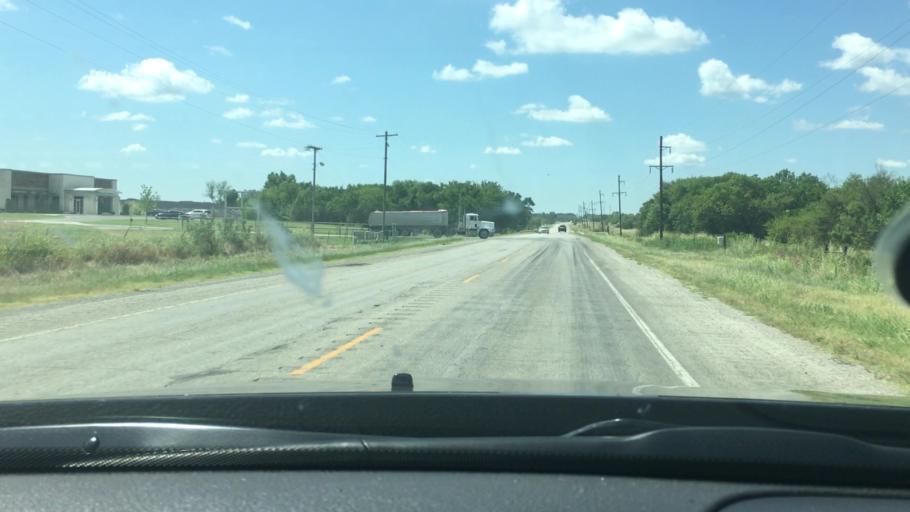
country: US
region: Oklahoma
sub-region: Carter County
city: Ardmore
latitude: 34.0797
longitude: -97.1429
